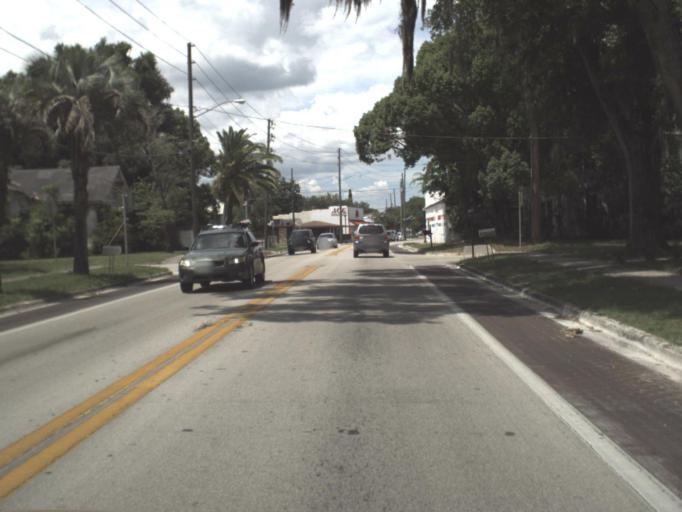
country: US
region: Florida
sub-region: Alachua County
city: High Springs
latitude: 29.8242
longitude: -82.5987
